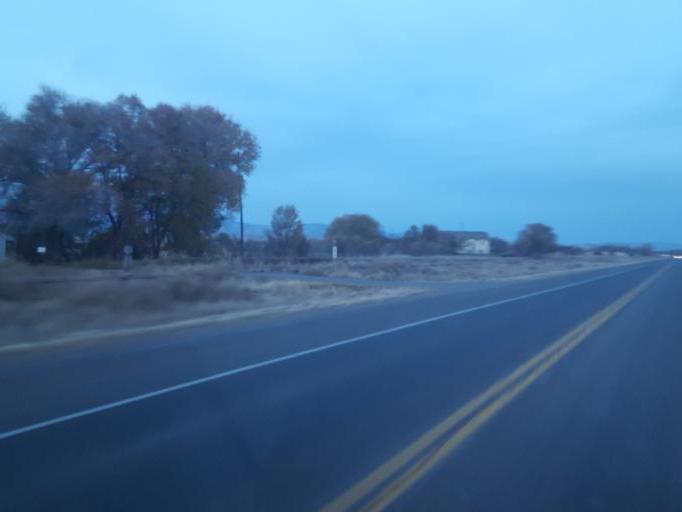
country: US
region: Colorado
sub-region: Rio Grande County
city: Monte Vista
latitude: 37.5700
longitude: -106.1186
